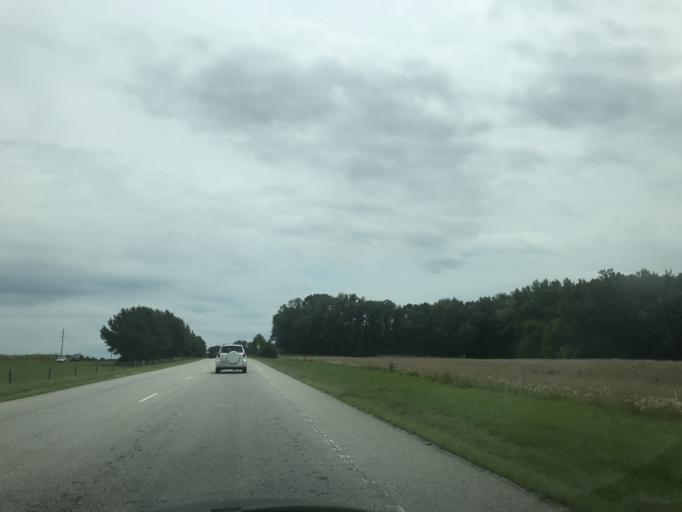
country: US
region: North Carolina
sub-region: Franklin County
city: Franklinton
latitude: 36.1660
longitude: -78.4512
